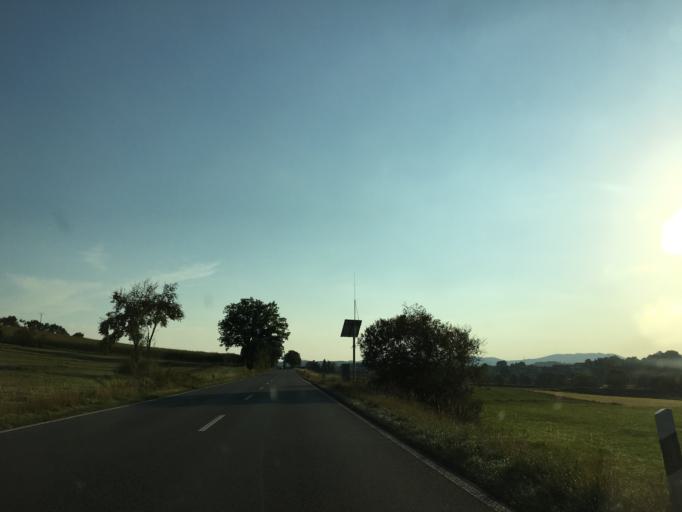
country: DE
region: Hesse
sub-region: Regierungsbezirk Giessen
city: Munchhausen
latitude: 50.9480
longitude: 8.7124
